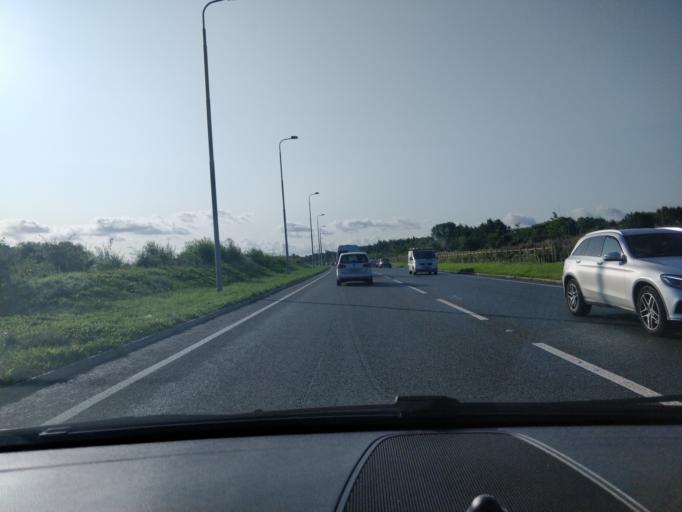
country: GB
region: England
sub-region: Sefton
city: Maghull
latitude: 53.4963
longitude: -2.9634
